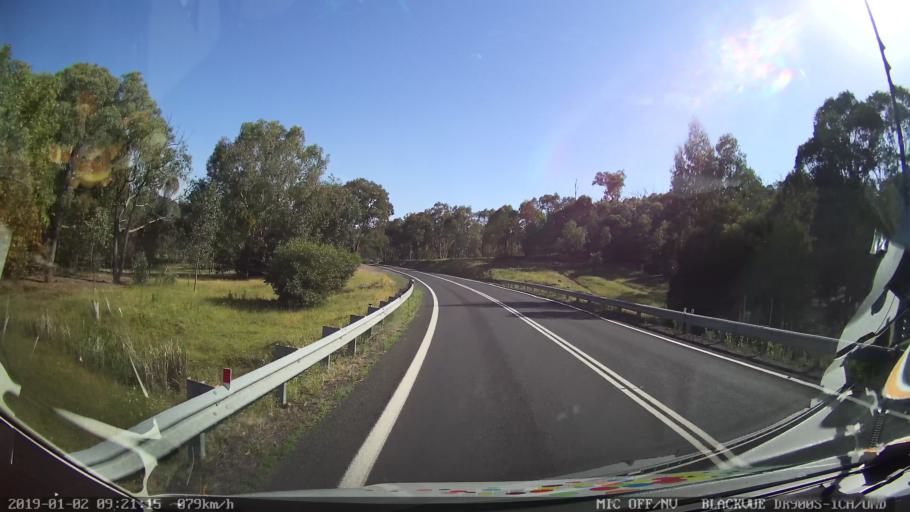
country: AU
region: New South Wales
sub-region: Tumut Shire
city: Tumut
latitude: -35.4080
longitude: 148.2909
